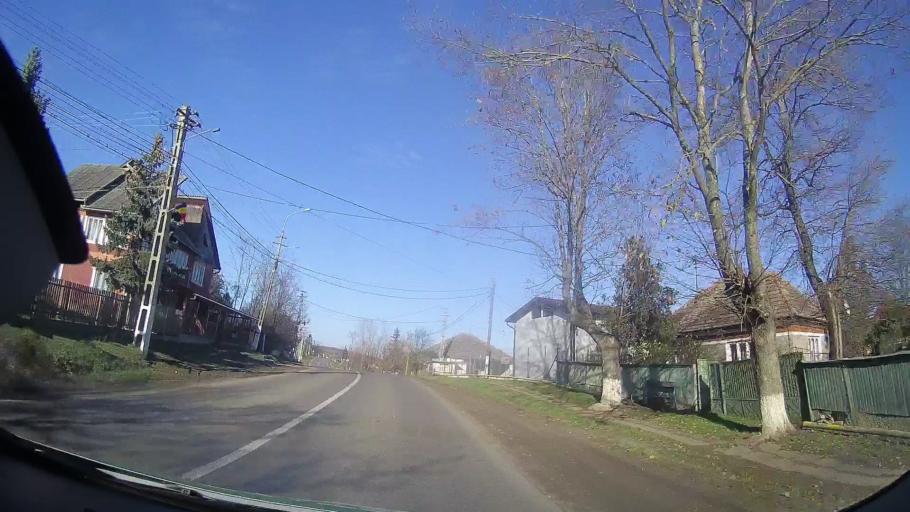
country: RO
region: Mures
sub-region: Comuna Mihesu de Campie
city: Mihesu de Campie
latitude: 46.6728
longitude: 24.1568
